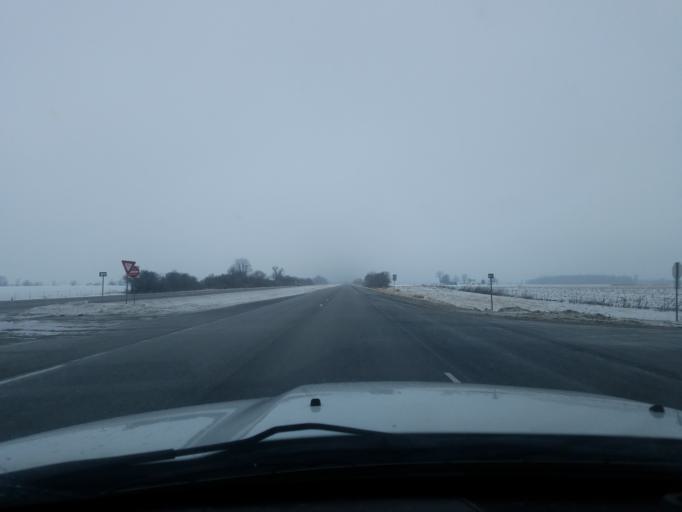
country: US
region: Indiana
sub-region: Fulton County
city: Rochester
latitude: 40.9822
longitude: -86.1679
